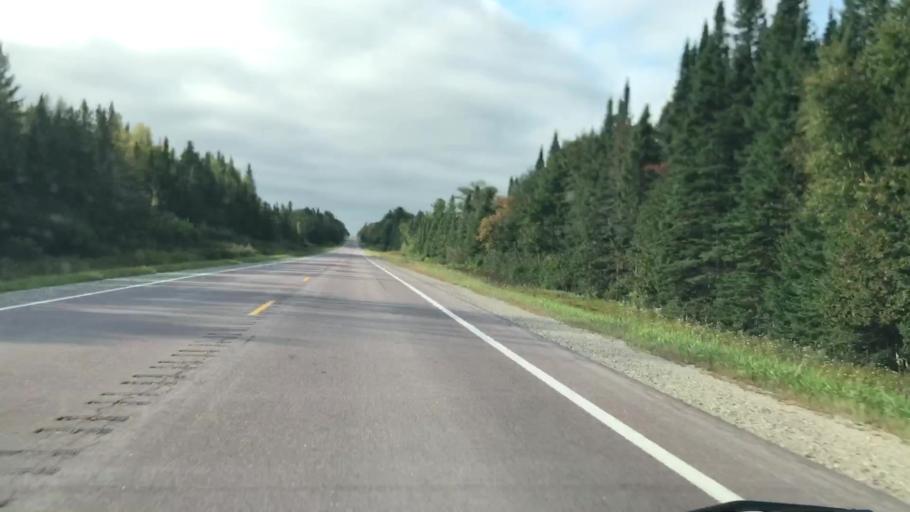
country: US
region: Michigan
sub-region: Luce County
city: Newberry
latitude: 46.2988
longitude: -85.5687
